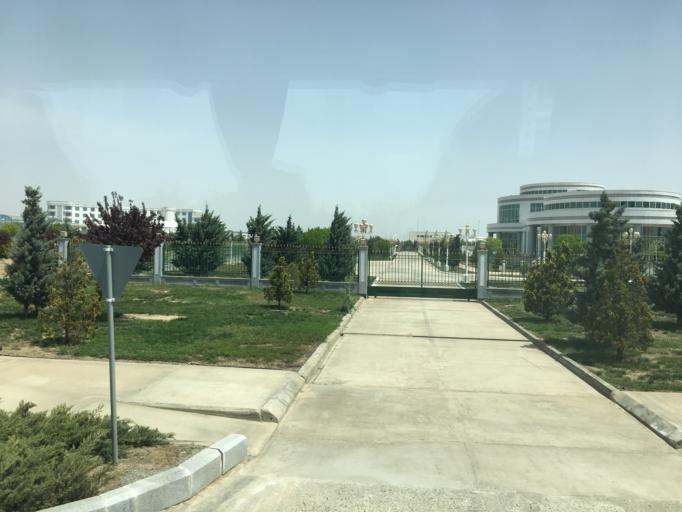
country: TM
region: Balkan
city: Turkmenbasy
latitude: 39.9817
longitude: 52.8265
